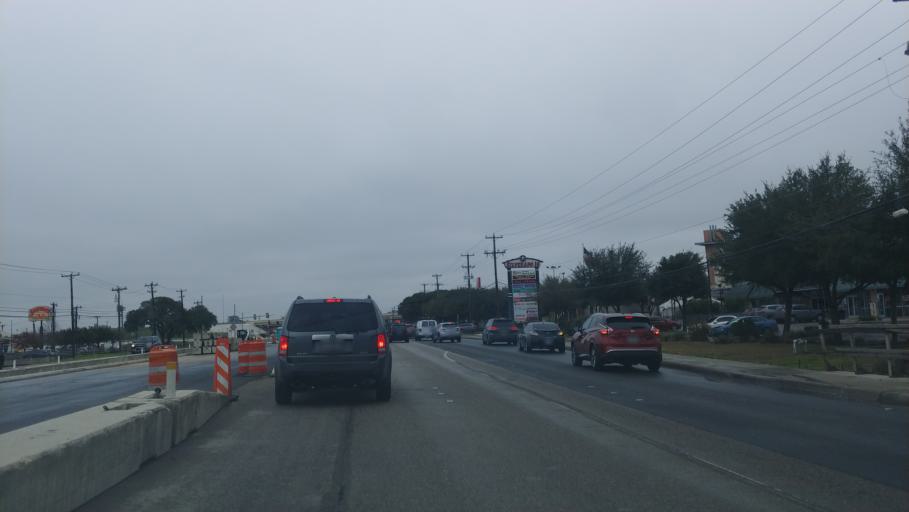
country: US
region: Texas
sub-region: Bexar County
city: Helotes
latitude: 29.5563
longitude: -98.6704
